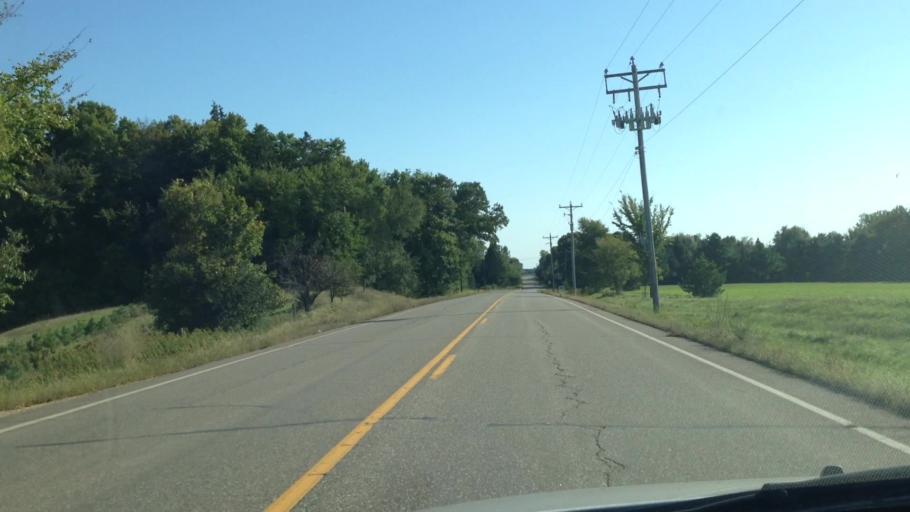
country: US
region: Minnesota
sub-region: Washington County
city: Stillwater
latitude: 45.0959
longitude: -92.8128
